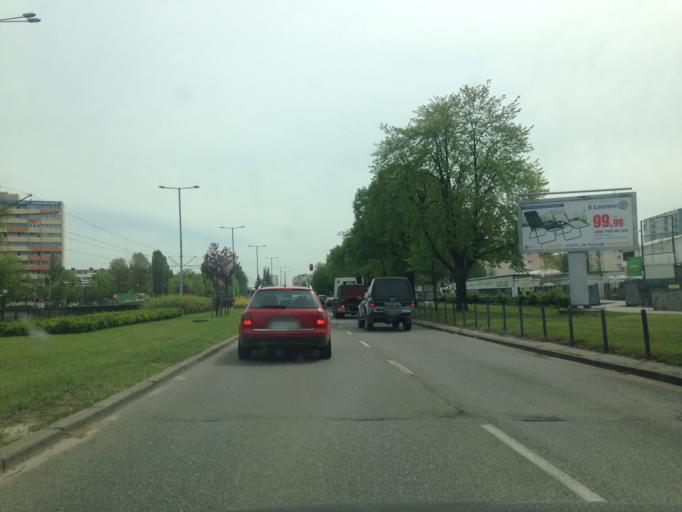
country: PL
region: Pomeranian Voivodeship
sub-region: Sopot
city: Sopot
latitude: 54.4137
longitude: 18.5873
